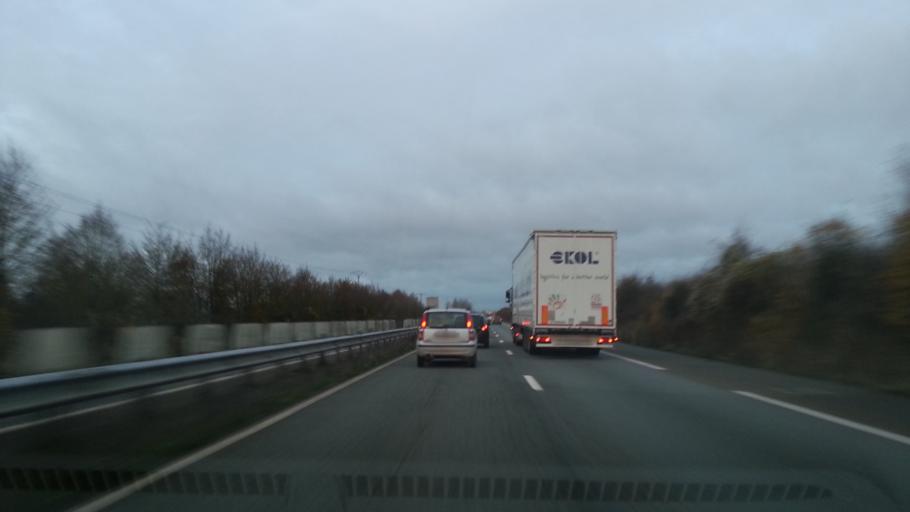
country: FR
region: Picardie
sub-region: Departement de l'Oise
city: Bresles
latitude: 49.4140
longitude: 2.2768
